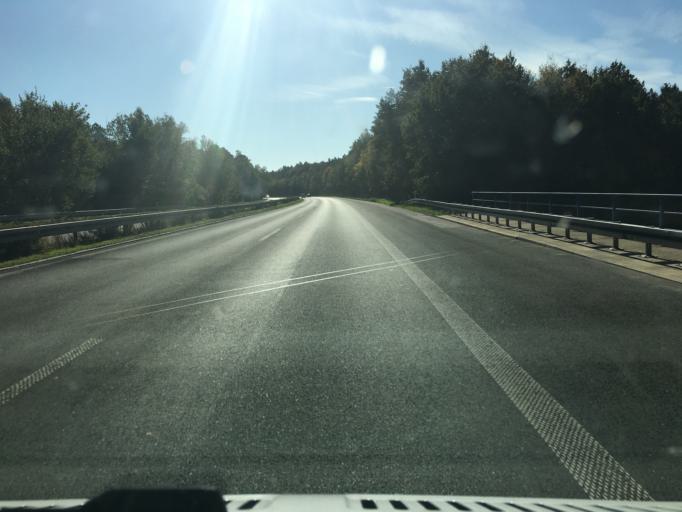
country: DE
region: Saxony
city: Dennheritz
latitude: 50.8003
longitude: 12.4550
